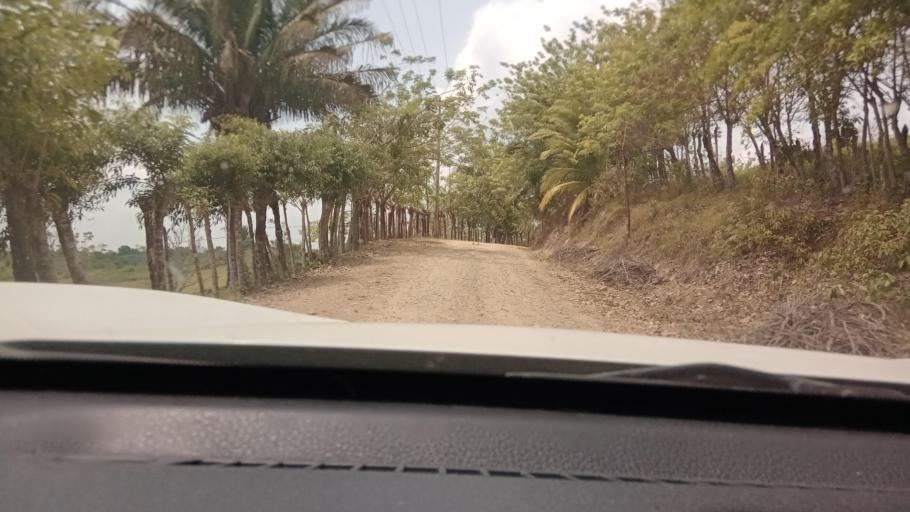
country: MX
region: Tabasco
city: Chontalpa
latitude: 17.5644
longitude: -93.7135
